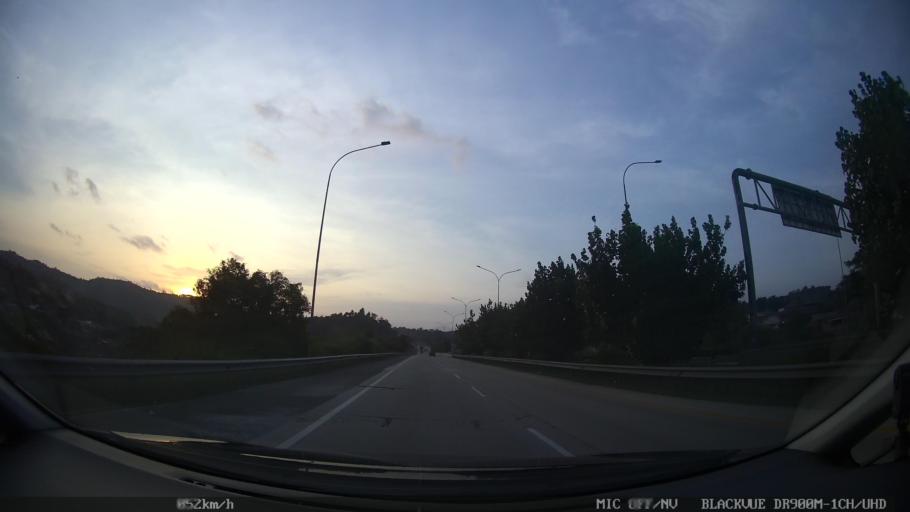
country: ID
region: Lampung
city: Penengahan
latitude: -5.8672
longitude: 105.7483
